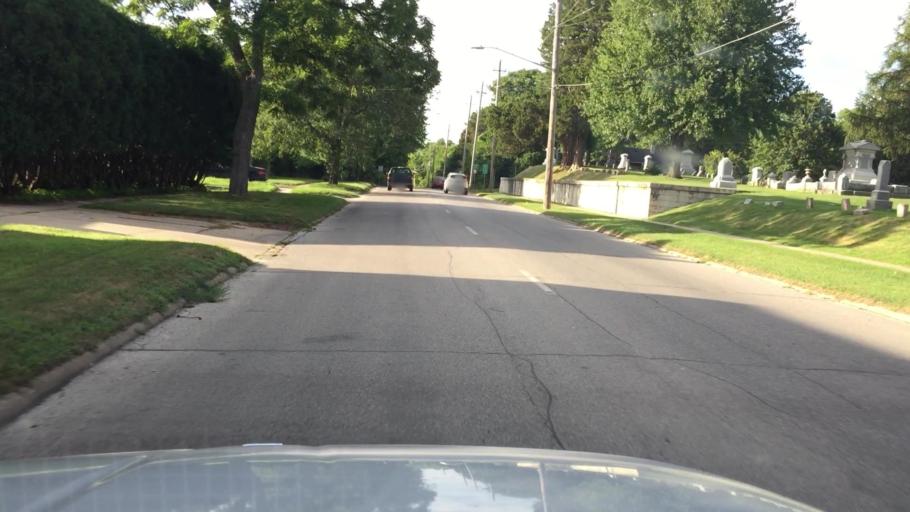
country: US
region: Iowa
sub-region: Johnson County
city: Iowa City
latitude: 41.6692
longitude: -91.5228
